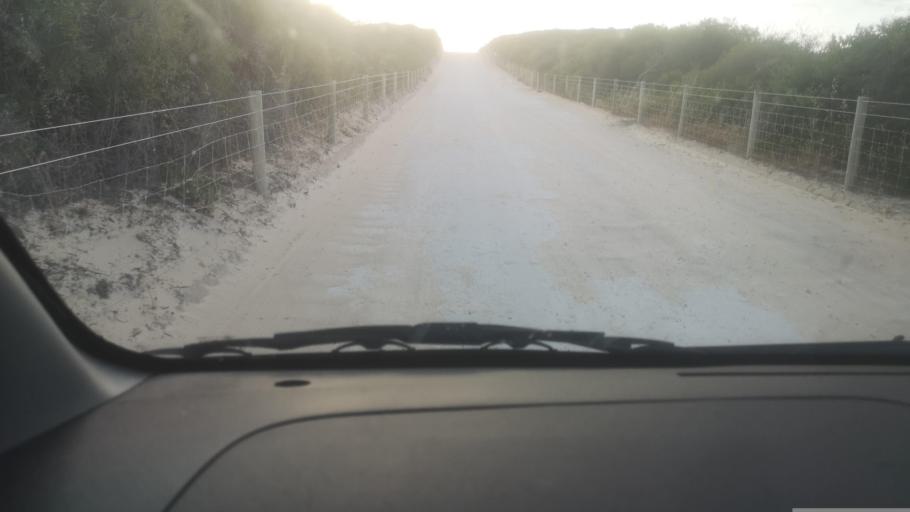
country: AU
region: Western Australia
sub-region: Wanneroo
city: Two Rocks
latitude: -31.5202
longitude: 115.6074
